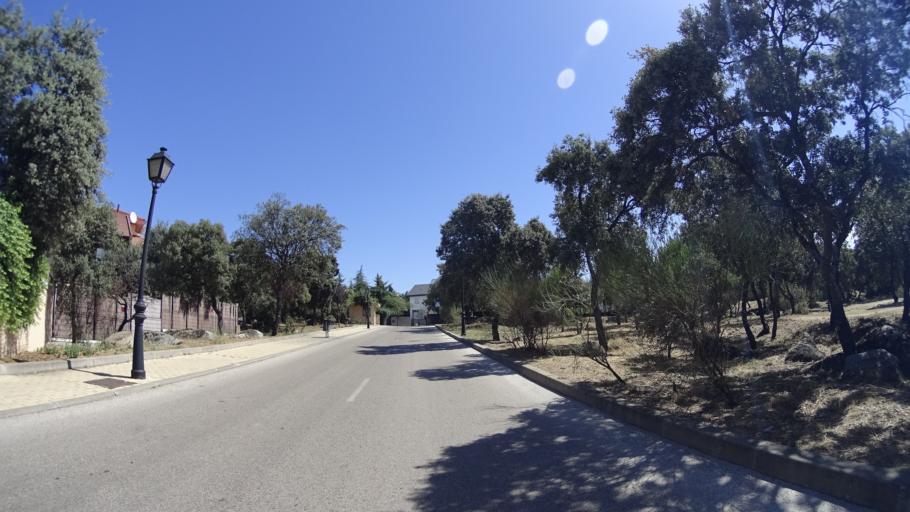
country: ES
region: Madrid
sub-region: Provincia de Madrid
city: Torrelodones
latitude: 40.5733
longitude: -3.9489
